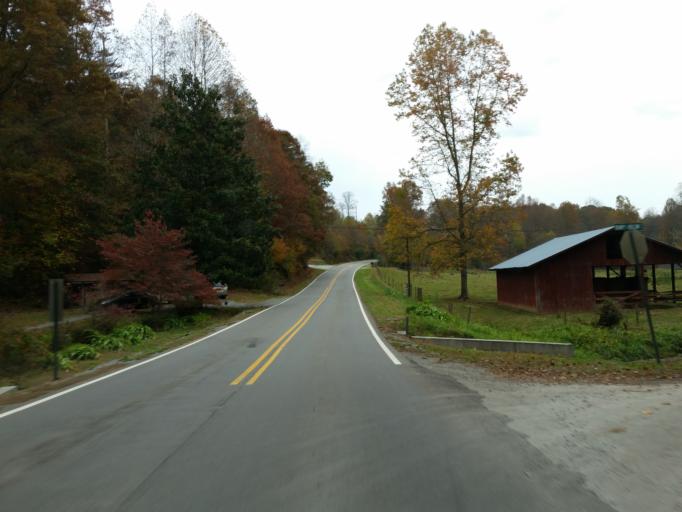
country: US
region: Georgia
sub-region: Gilmer County
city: Ellijay
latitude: 34.6609
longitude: -84.3786
